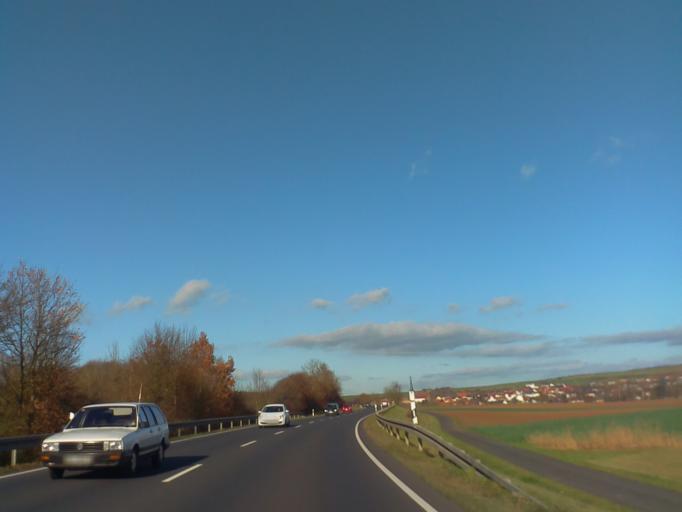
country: DE
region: Bavaria
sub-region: Regierungsbezirk Unterfranken
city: Wuelfershausen
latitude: 50.3209
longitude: 10.3448
